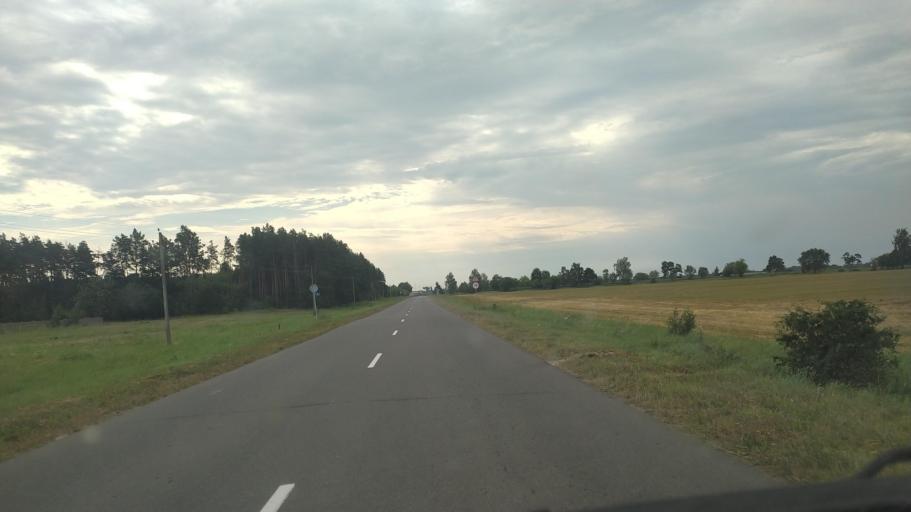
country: BY
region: Brest
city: Byaroza
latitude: 52.5604
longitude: 24.9098
